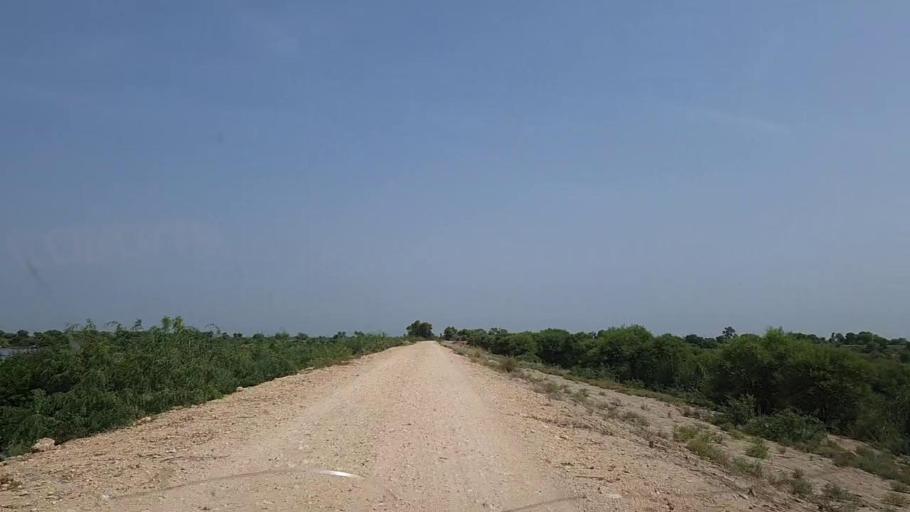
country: PK
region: Sindh
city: Ghotki
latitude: 28.0911
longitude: 69.4088
